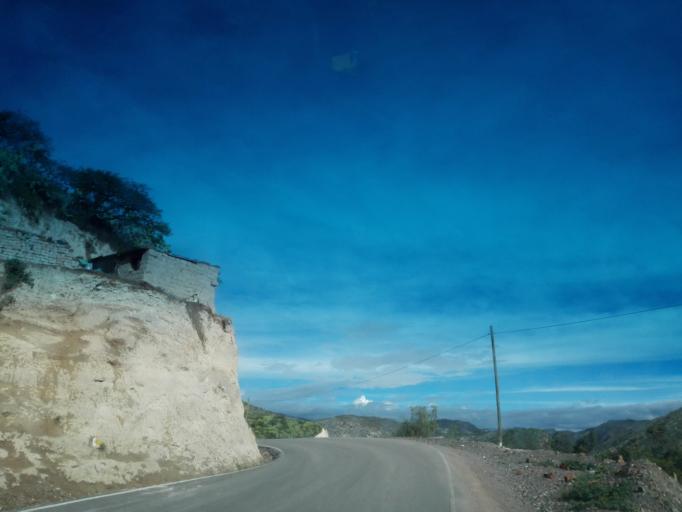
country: PE
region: Ayacucho
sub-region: Provincia de Huamanga
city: Pacaycasa
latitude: -13.0757
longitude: -74.2401
